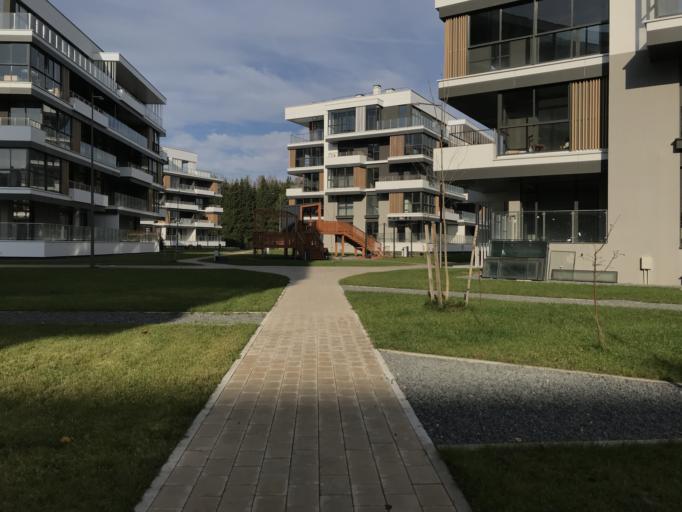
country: BY
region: Minsk
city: Khatsyezhyna
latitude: 53.9468
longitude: 27.3315
